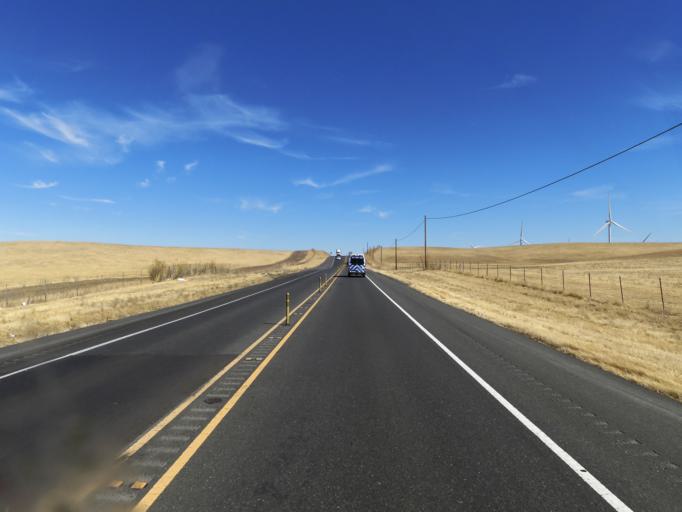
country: US
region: California
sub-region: Solano County
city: Rio Vista
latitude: 38.1837
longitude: -121.8311
